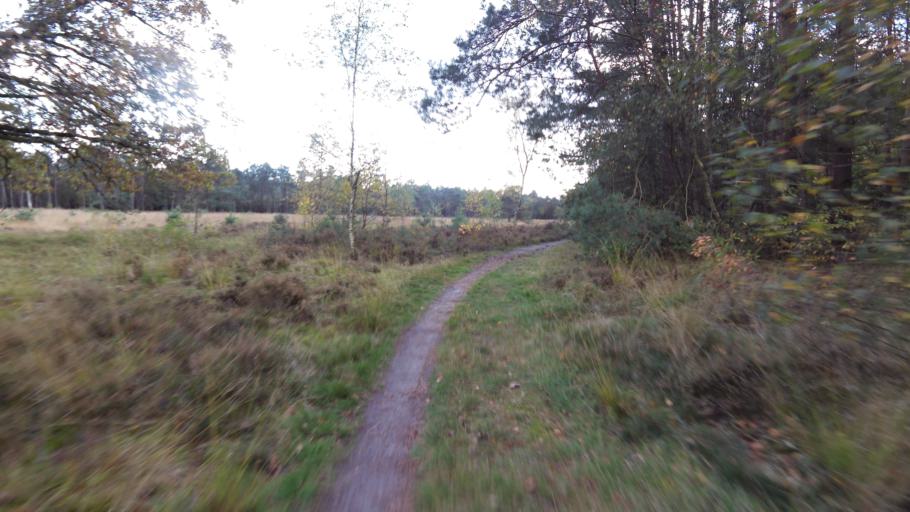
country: NL
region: Gelderland
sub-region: Gemeente Nunspeet
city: Nunspeet
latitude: 52.3643
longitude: 5.8310
